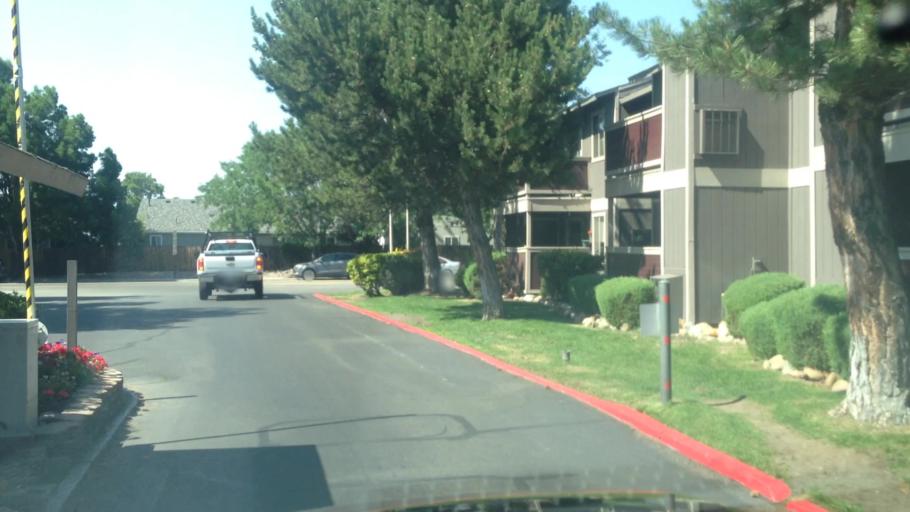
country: US
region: Nevada
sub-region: Washoe County
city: Sparks
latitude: 39.4856
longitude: -119.7445
